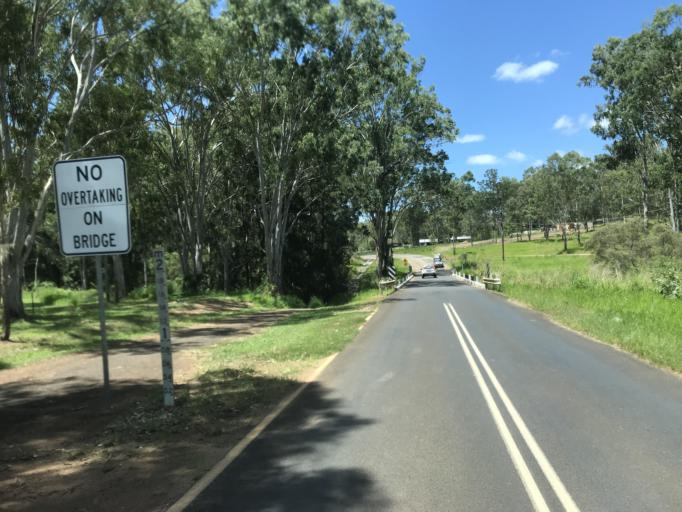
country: AU
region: Queensland
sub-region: Tablelands
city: Atherton
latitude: -17.4136
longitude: 145.3928
